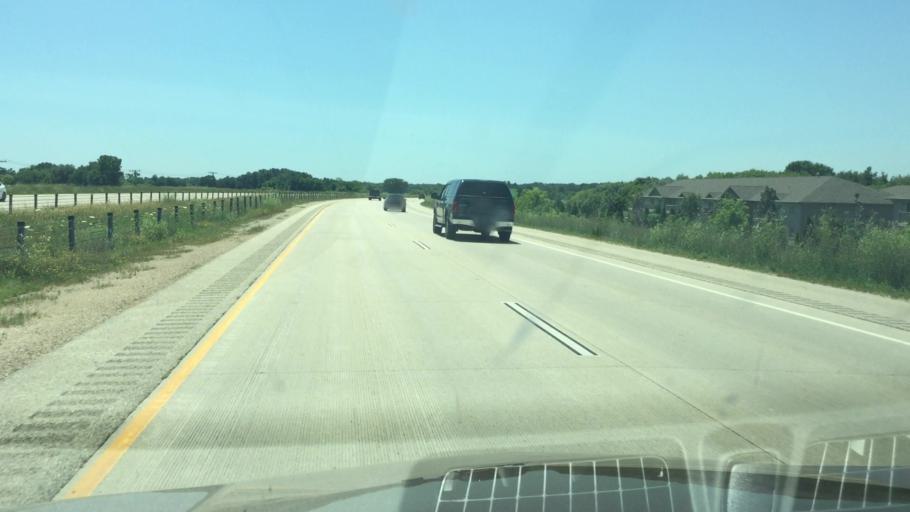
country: US
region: Wisconsin
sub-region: Dodge County
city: Beaver Dam
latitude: 43.4403
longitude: -88.8262
